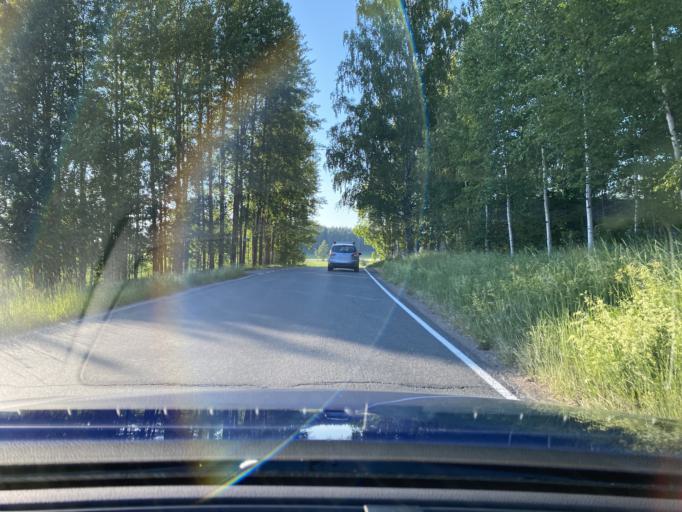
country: FI
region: Haeme
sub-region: Haemeenlinna
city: Tervakoski
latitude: 60.7327
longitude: 24.6705
